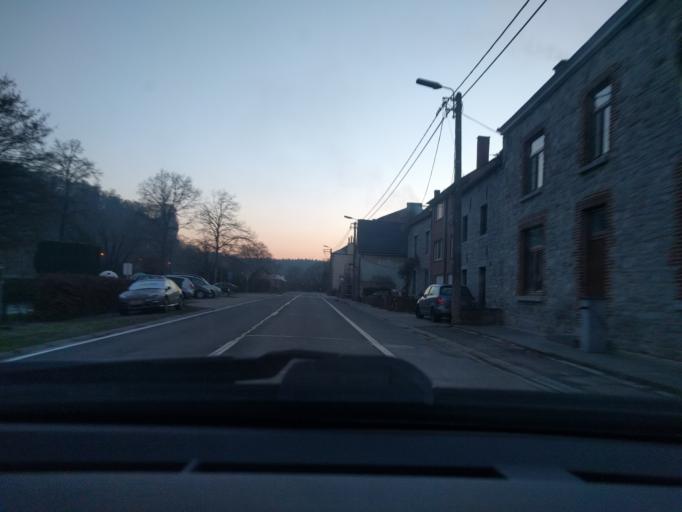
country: BE
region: Wallonia
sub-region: Province de Namur
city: Namur
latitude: 50.4729
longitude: 4.9303
